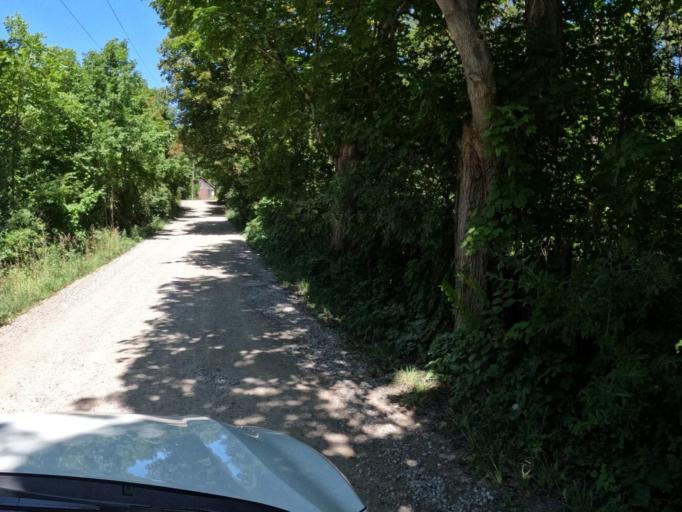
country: CA
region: Ontario
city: Cambridge
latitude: 43.4064
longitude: -80.2608
